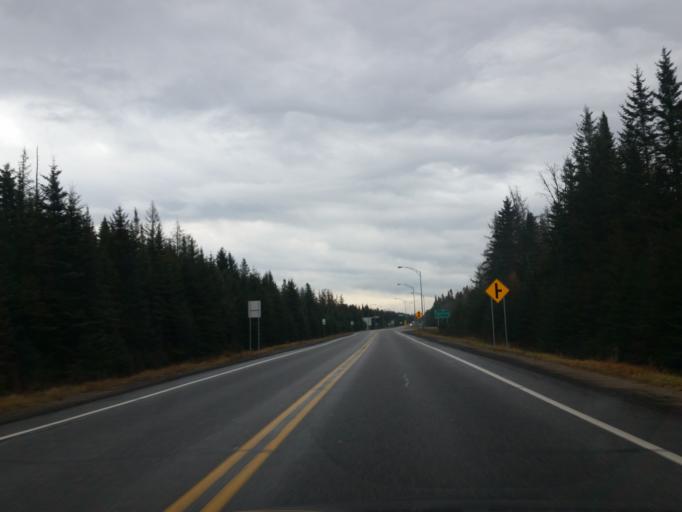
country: CA
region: Quebec
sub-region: Capitale-Nationale
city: Shannon
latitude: 46.8811
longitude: -71.4716
